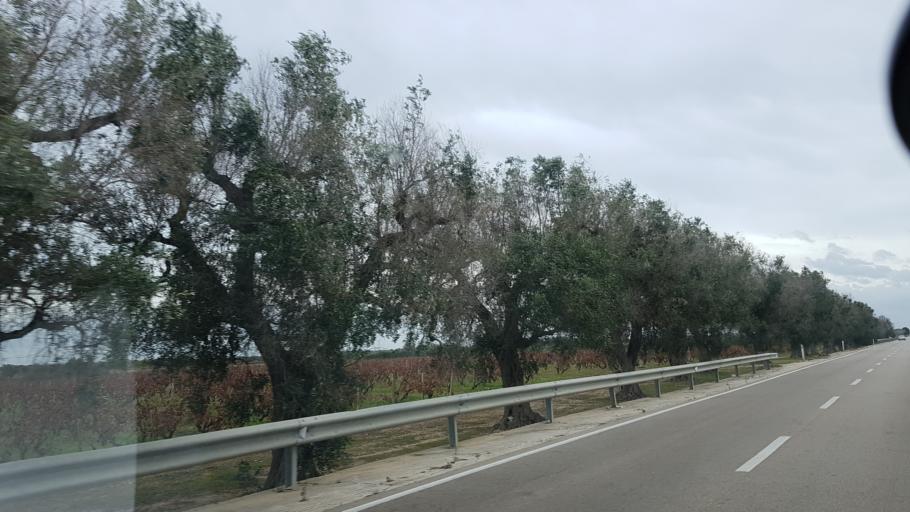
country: IT
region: Apulia
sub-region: Provincia di Brindisi
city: San Donaci
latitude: 40.4049
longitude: 17.8950
